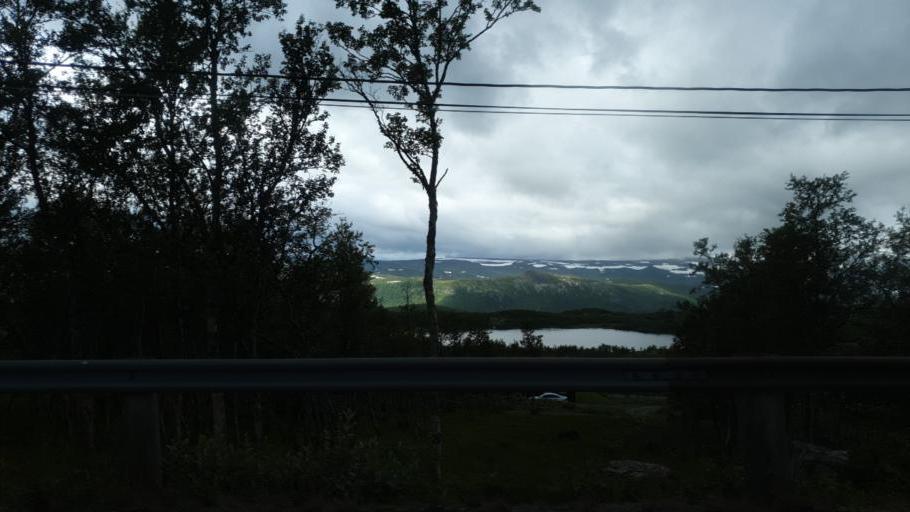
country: NO
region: Oppland
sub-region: Vestre Slidre
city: Slidre
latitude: 61.2637
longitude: 8.8695
